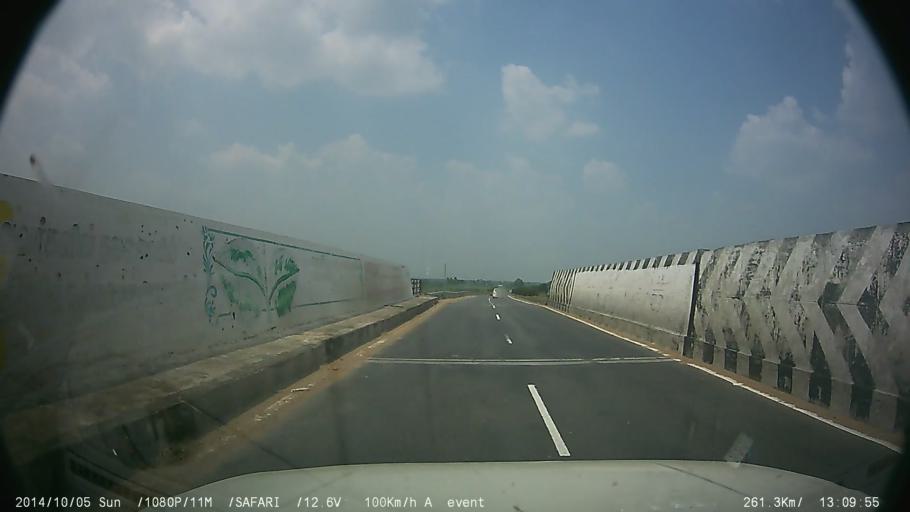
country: IN
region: Tamil Nadu
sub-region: Villupuram
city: Villupuram
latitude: 11.9365
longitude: 79.4732
